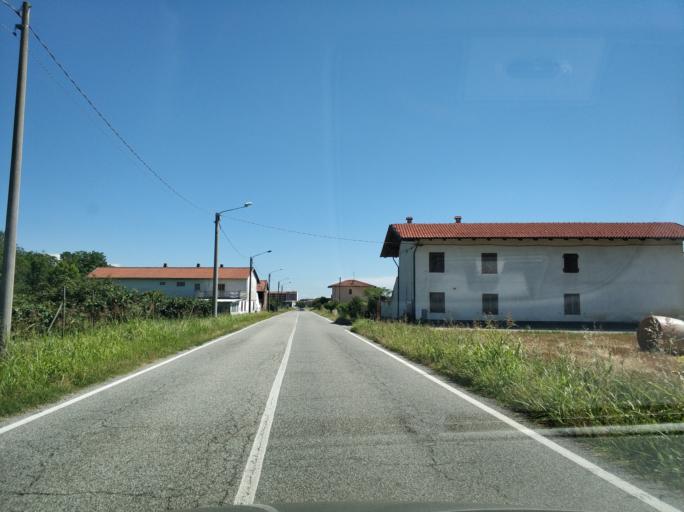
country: IT
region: Piedmont
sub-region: Provincia di Vercelli
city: Cigliano
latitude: 45.3182
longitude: 8.0183
